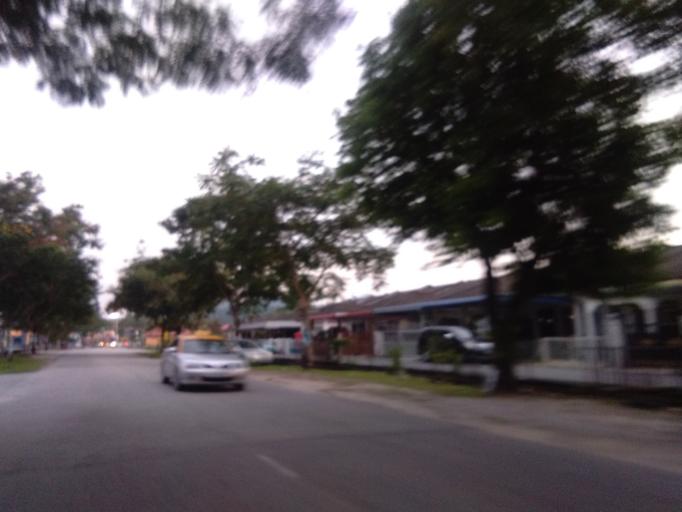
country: MY
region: Kedah
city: Kulim
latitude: 5.3743
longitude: 100.5568
